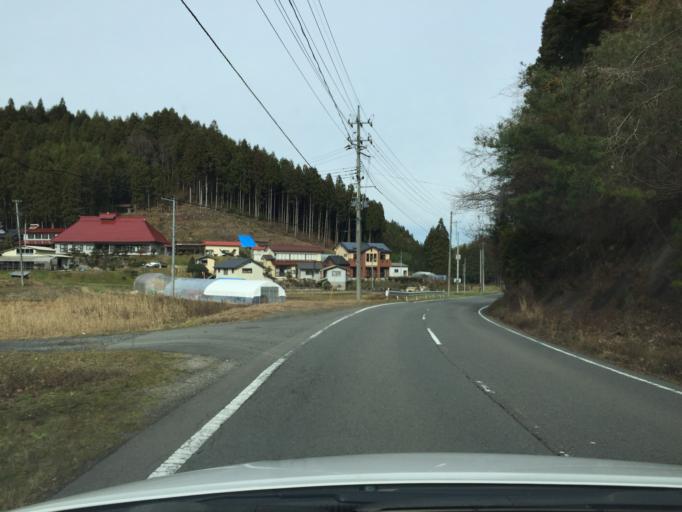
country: JP
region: Fukushima
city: Ishikawa
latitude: 37.2048
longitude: 140.6265
